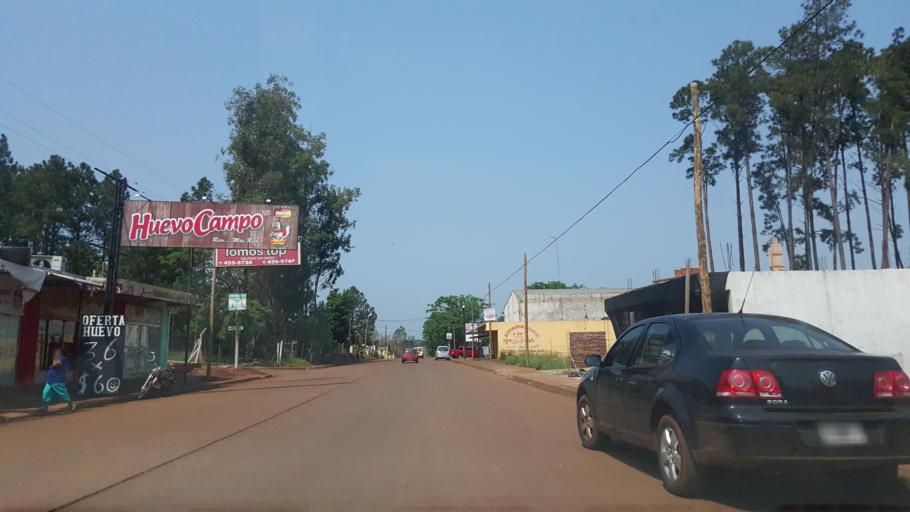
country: AR
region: Misiones
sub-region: Departamento de Capital
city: Posadas
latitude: -27.4165
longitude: -55.9567
